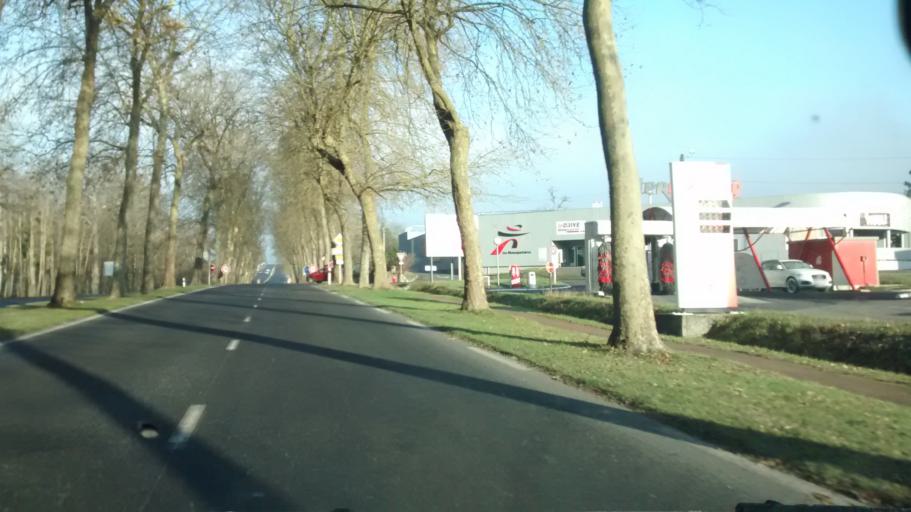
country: FR
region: Centre
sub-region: Departement d'Indre-et-Loire
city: Montbazon
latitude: 47.2920
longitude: 0.7186
